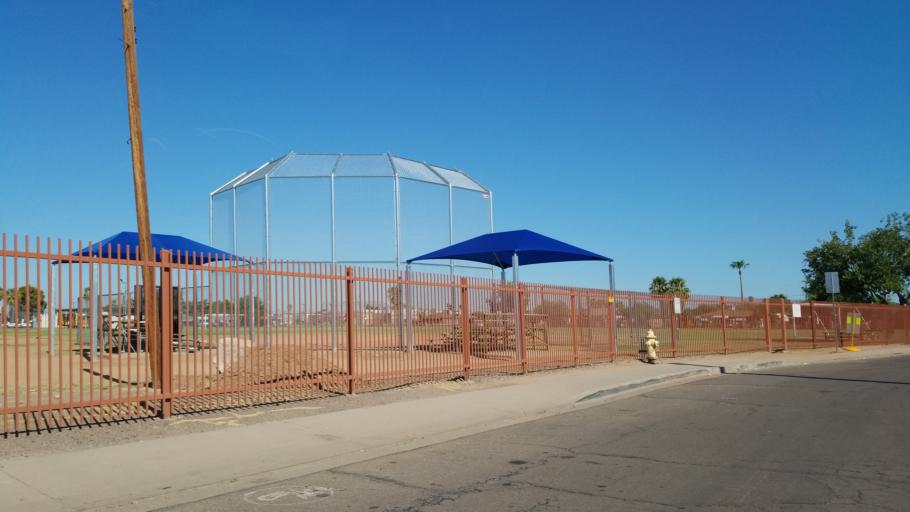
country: US
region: Arizona
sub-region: Maricopa County
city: Phoenix
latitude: 33.4683
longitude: -112.1323
